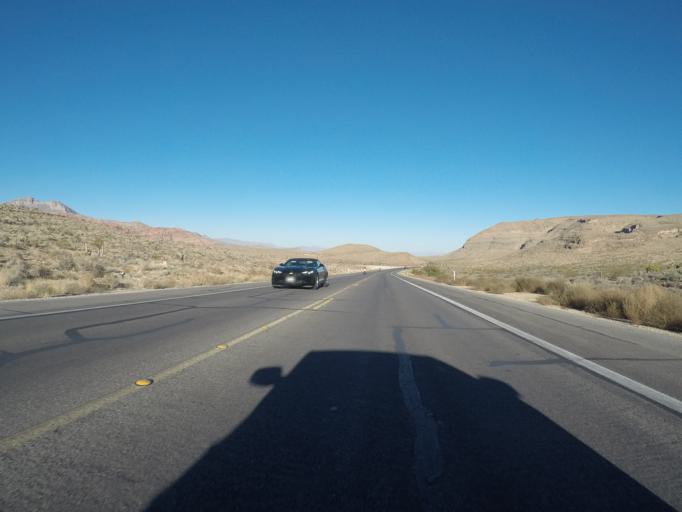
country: US
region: Nevada
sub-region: Clark County
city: Summerlin South
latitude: 36.1179
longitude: -115.4427
